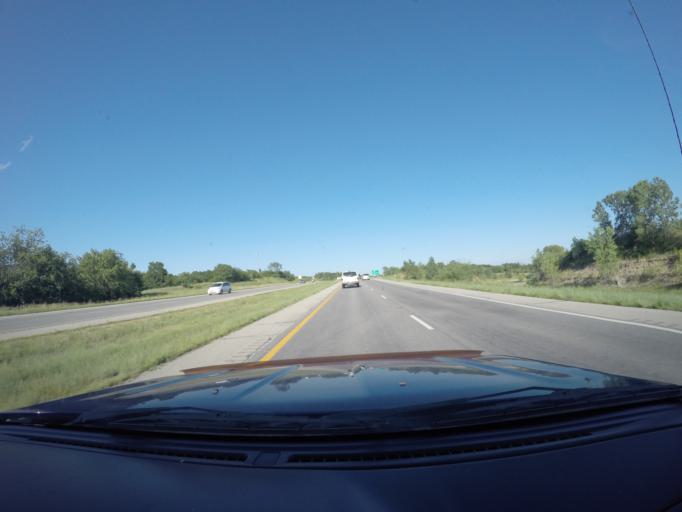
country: US
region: Kansas
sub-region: Shawnee County
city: Topeka
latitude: 39.0934
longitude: -95.6108
